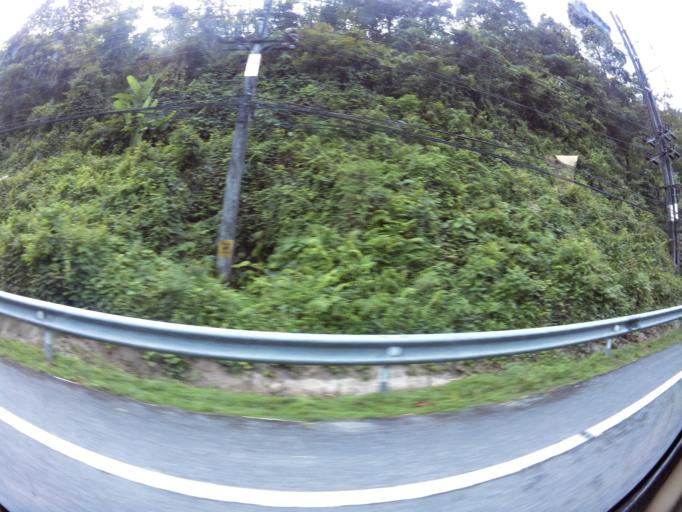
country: TH
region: Phuket
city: Patong
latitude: 7.9392
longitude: 98.2773
